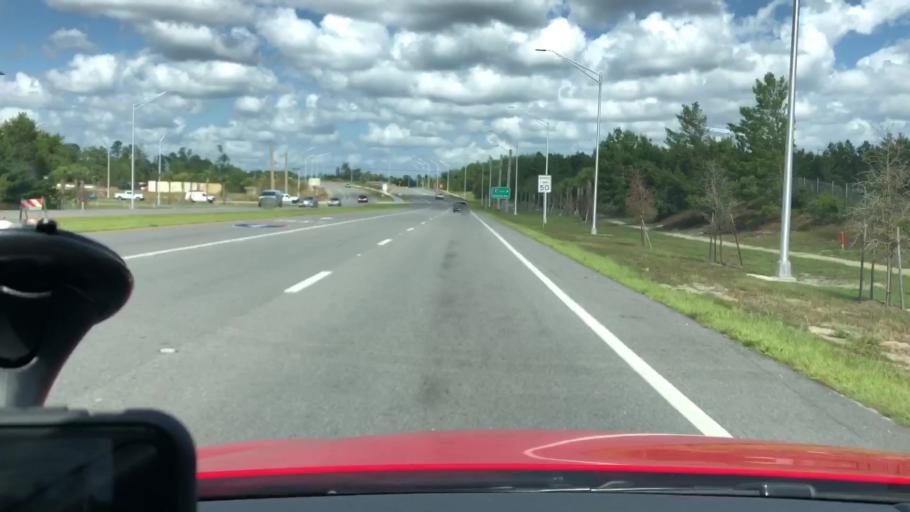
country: US
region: Florida
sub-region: Volusia County
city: Lake Helen
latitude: 28.9511
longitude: -81.2537
